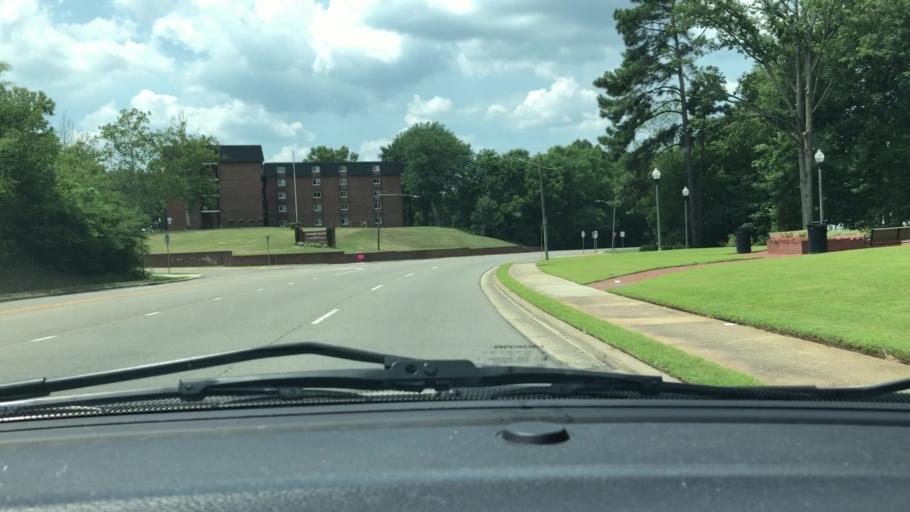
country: US
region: North Carolina
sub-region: Lee County
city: Sanford
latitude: 35.4731
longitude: -79.1769
